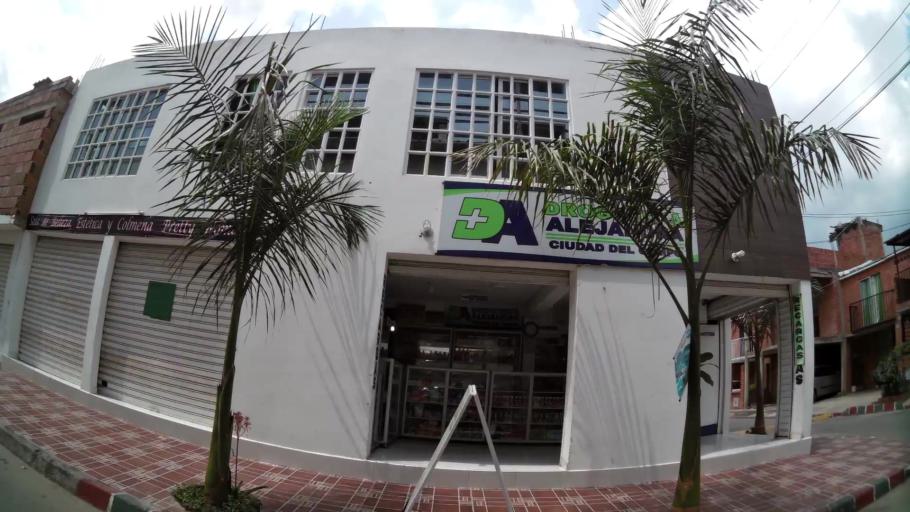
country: CO
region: Valle del Cauca
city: Cali
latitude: 3.4601
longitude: -76.4624
